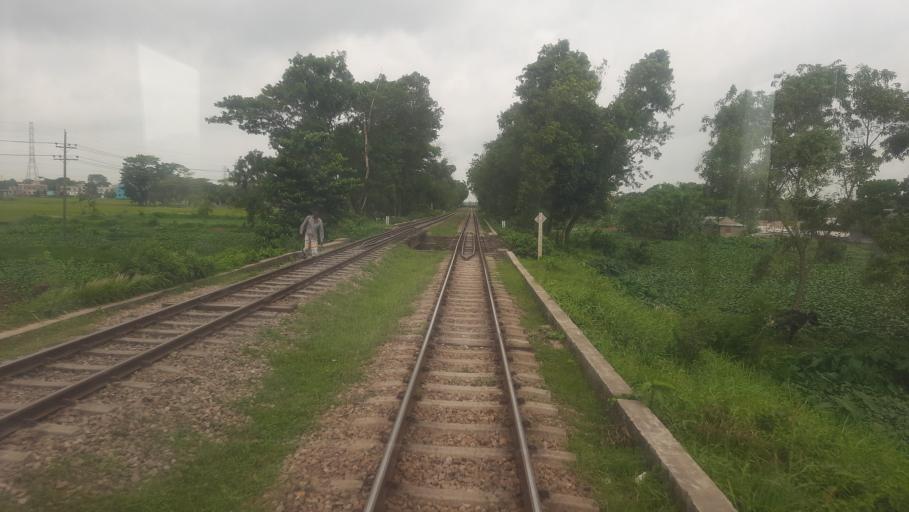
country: BD
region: Dhaka
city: Bhairab Bazar
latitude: 23.9663
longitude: 91.1006
